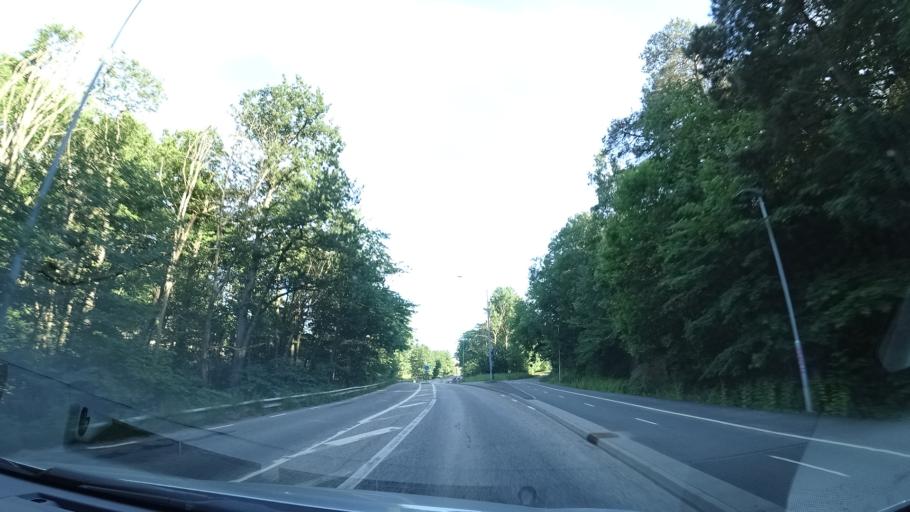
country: SE
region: Vaestra Goetaland
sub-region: Goteborg
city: Billdal
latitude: 57.5954
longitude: 11.9488
